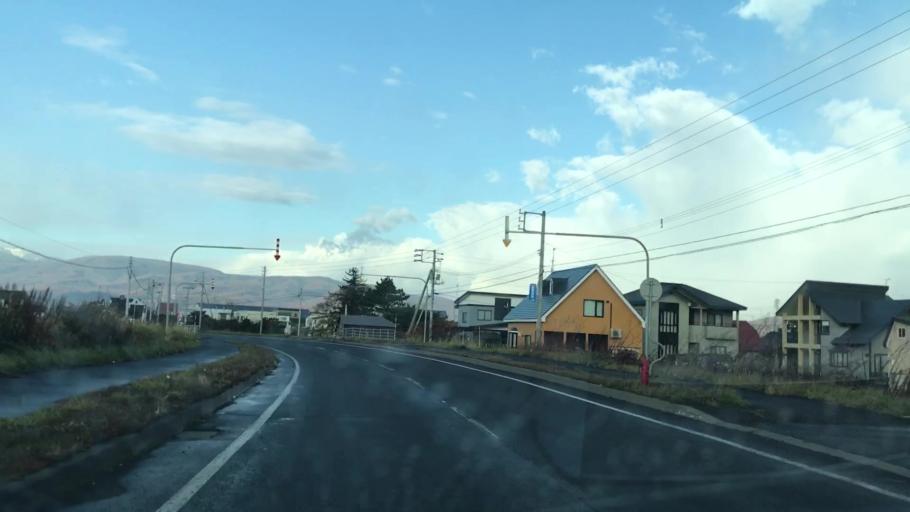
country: JP
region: Hokkaido
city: Yoichi
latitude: 43.1826
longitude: 140.8177
